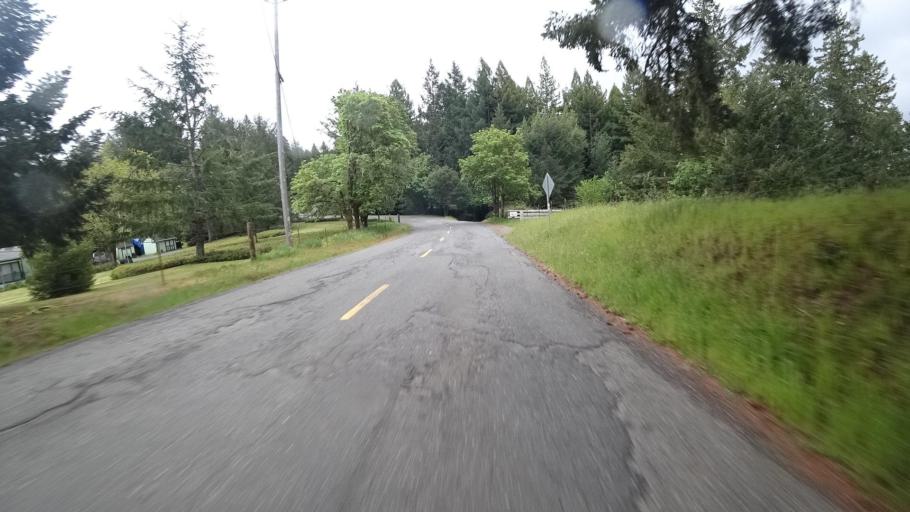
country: US
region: California
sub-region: Humboldt County
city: Redway
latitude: 40.2838
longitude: -123.7987
